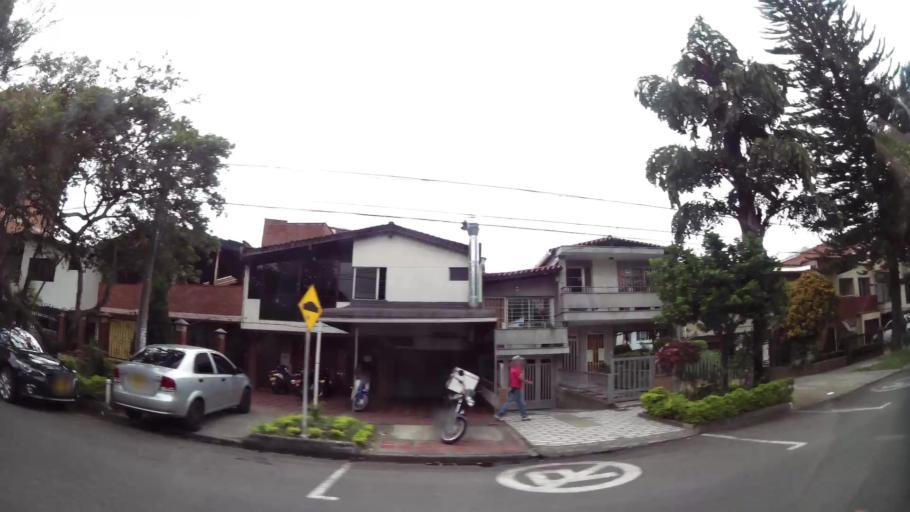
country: CO
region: Antioquia
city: Medellin
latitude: 6.2667
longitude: -75.5951
